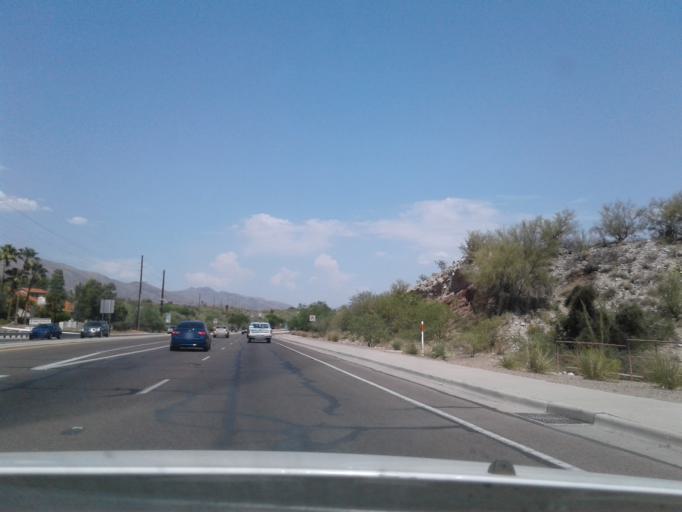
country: US
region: Arizona
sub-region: Pima County
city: Catalina Foothills
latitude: 32.3226
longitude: -110.9255
